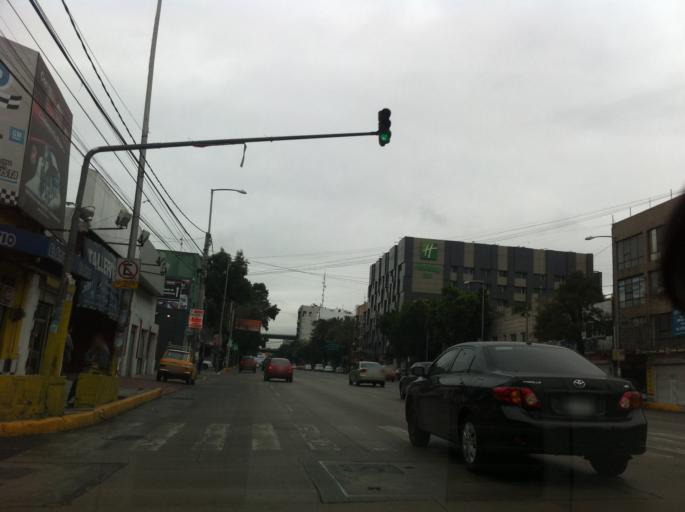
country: MX
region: Mexico City
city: Colonia del Valle
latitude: 19.3890
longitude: -99.1861
